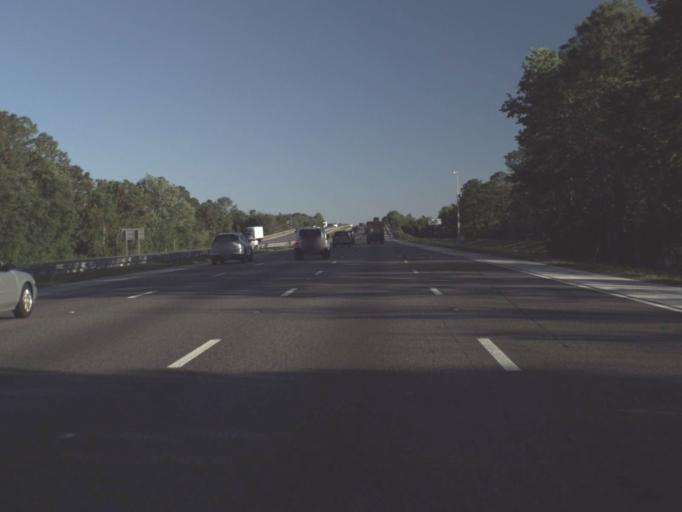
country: US
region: Florida
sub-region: Flagler County
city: Flagler Beach
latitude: 29.5024
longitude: -81.1940
